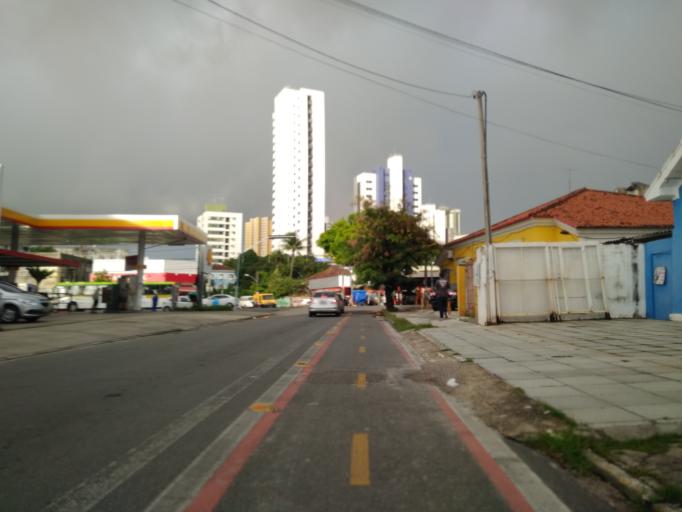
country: BR
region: Pernambuco
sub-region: Recife
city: Recife
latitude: -8.0361
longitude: -34.8918
